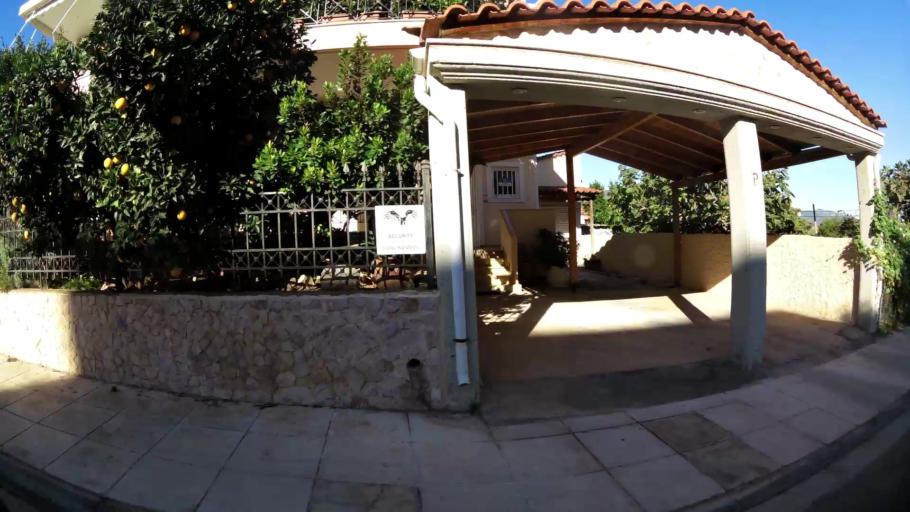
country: GR
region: Attica
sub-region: Nomarchia Anatolikis Attikis
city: Koropi
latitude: 37.9010
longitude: 23.8628
